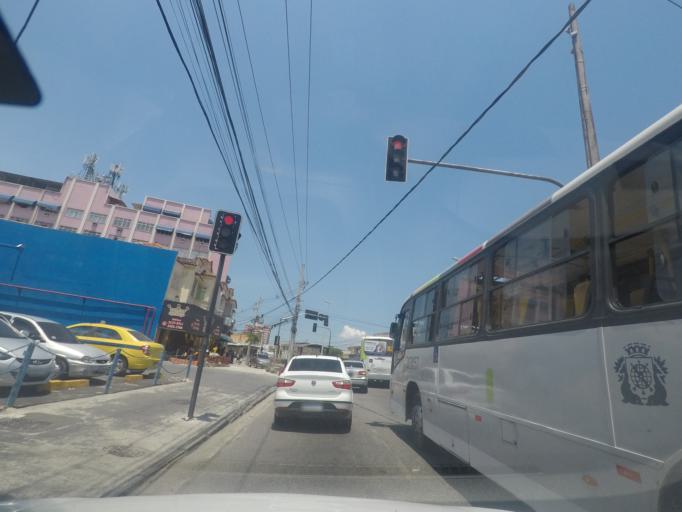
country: BR
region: Rio de Janeiro
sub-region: Duque De Caxias
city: Duque de Caxias
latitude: -22.8394
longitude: -43.2963
